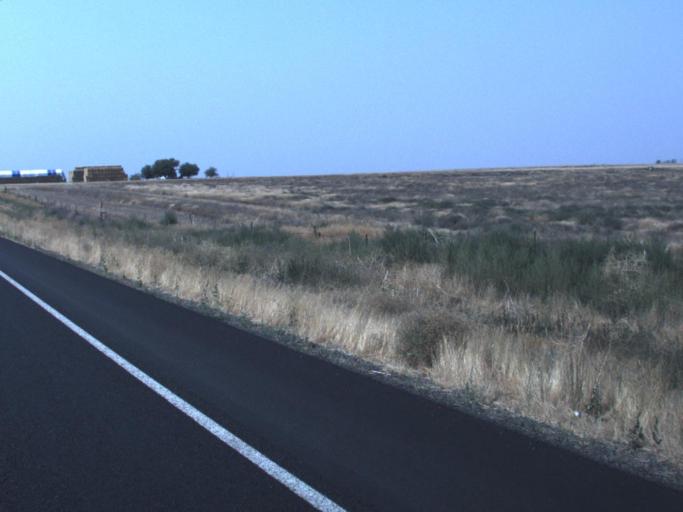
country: US
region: Washington
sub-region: Yakima County
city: Zillah
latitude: 46.5058
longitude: -120.1611
